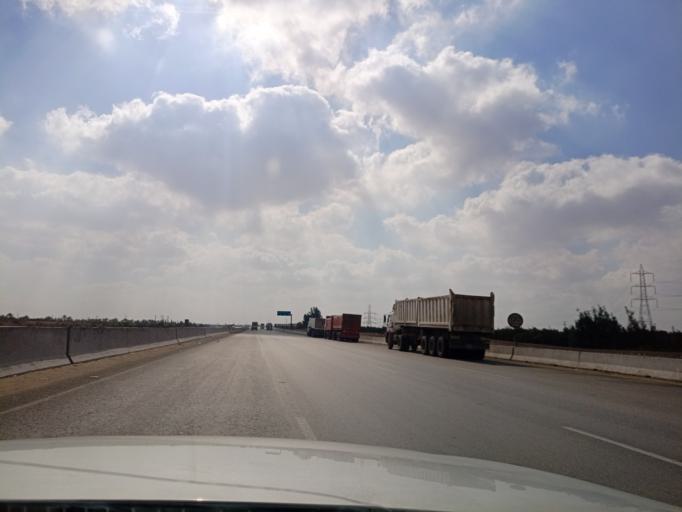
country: EG
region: Eastern Province
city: Bilbays
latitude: 30.3506
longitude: 31.5544
